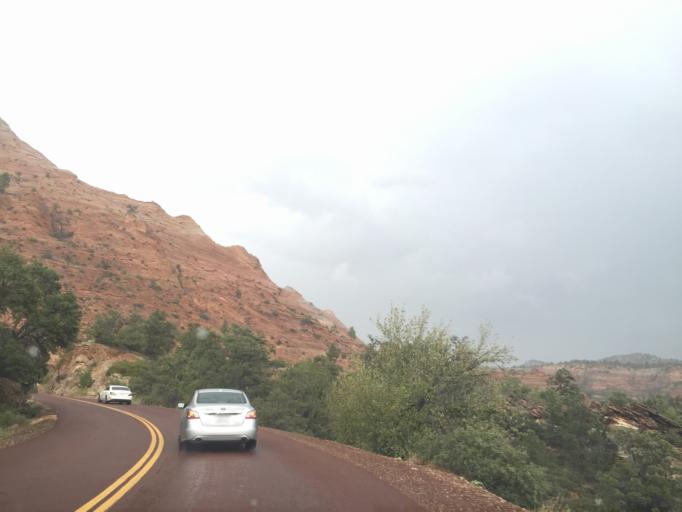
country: US
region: Utah
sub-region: Washington County
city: Hildale
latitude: 37.2159
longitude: -112.9295
